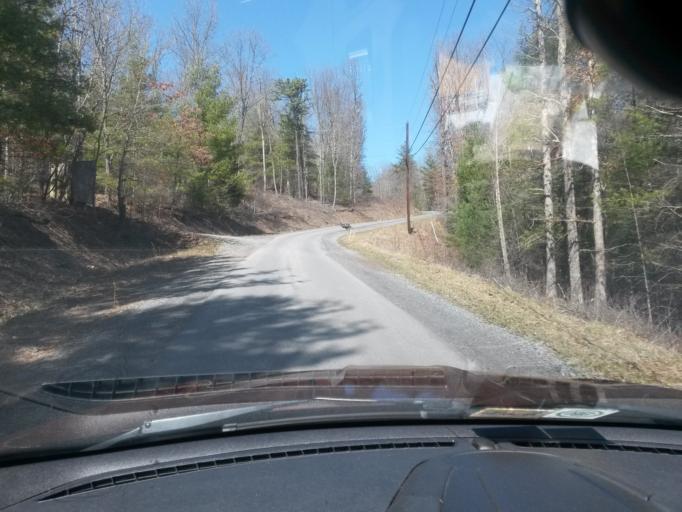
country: US
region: West Virginia
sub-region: Greenbrier County
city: White Sulphur Springs
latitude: 37.6696
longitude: -80.3181
